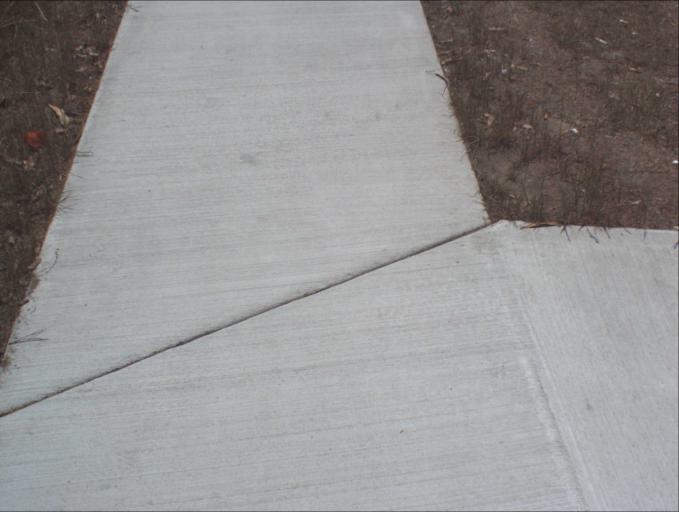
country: AU
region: Queensland
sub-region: Logan
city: Beenleigh
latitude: -27.7051
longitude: 153.2070
